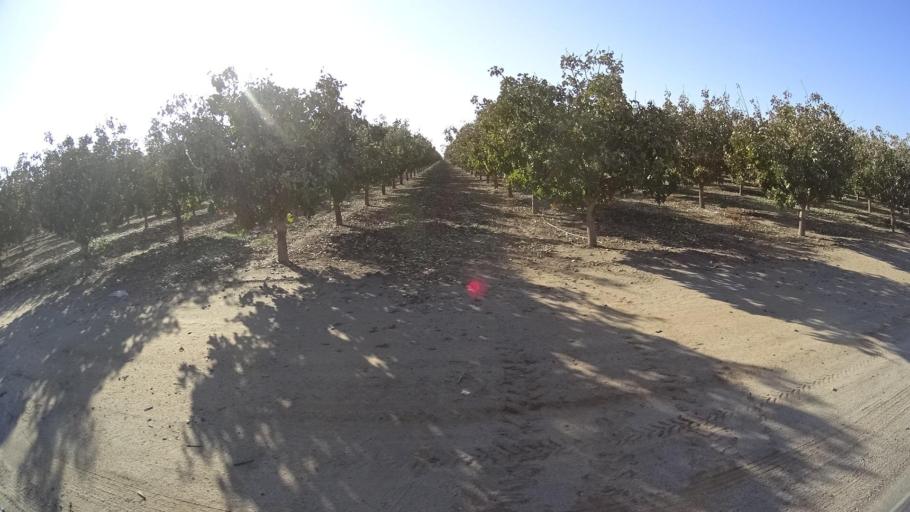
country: US
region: California
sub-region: Tulare County
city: Richgrove
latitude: 35.7327
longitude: -119.1216
